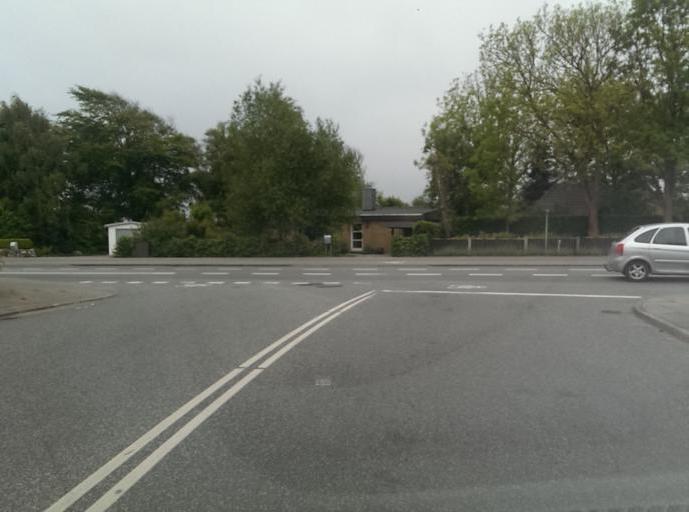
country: DK
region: South Denmark
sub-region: Fano Kommune
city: Nordby
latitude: 55.5157
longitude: 8.3711
